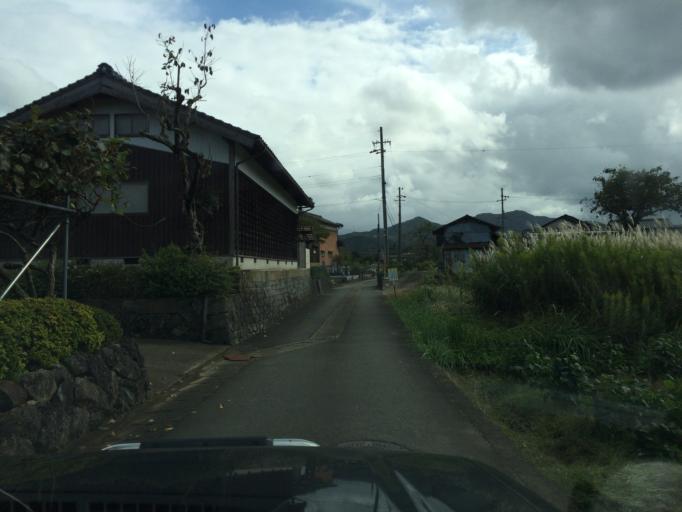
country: JP
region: Hyogo
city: Toyooka
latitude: 35.4966
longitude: 134.8063
